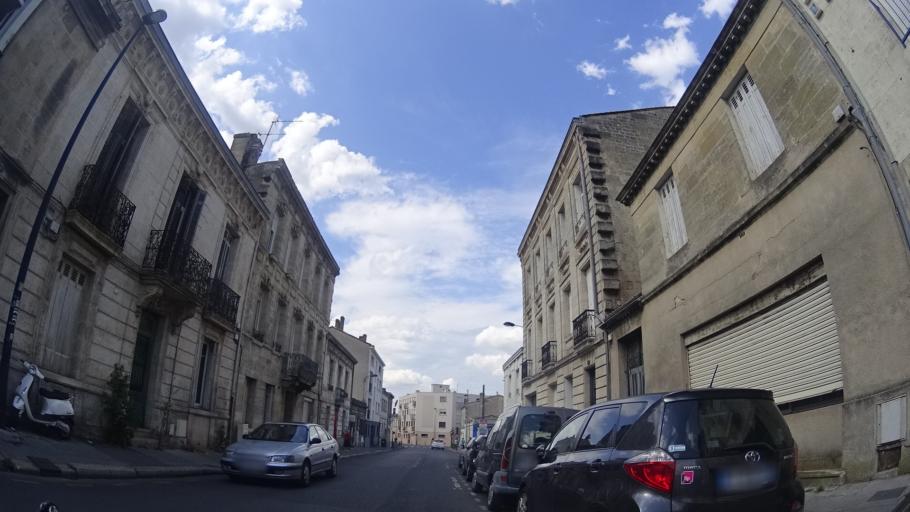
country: FR
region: Aquitaine
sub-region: Departement de la Gironde
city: Begles
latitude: 44.8228
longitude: -0.5658
